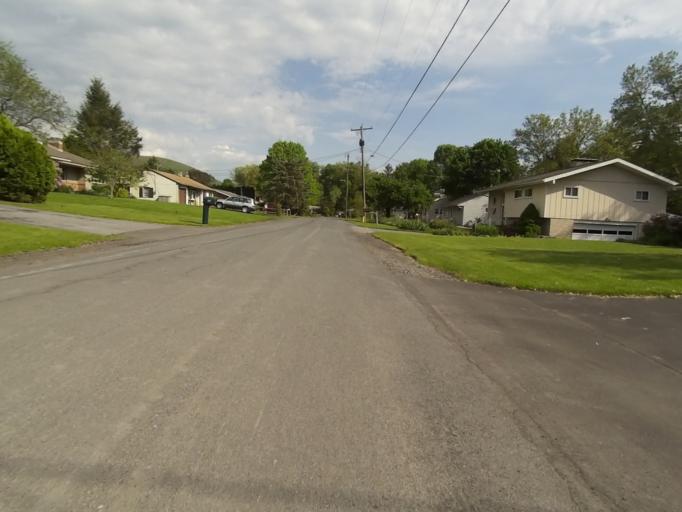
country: US
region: Pennsylvania
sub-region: Centre County
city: Houserville
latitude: 40.8250
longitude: -77.8284
